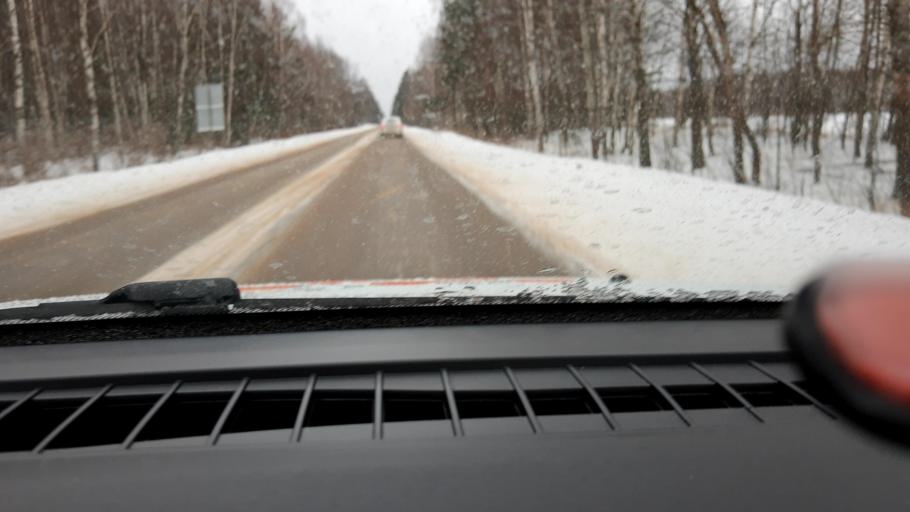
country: RU
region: Nizjnij Novgorod
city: Kstovo
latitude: 56.2945
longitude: 44.2788
